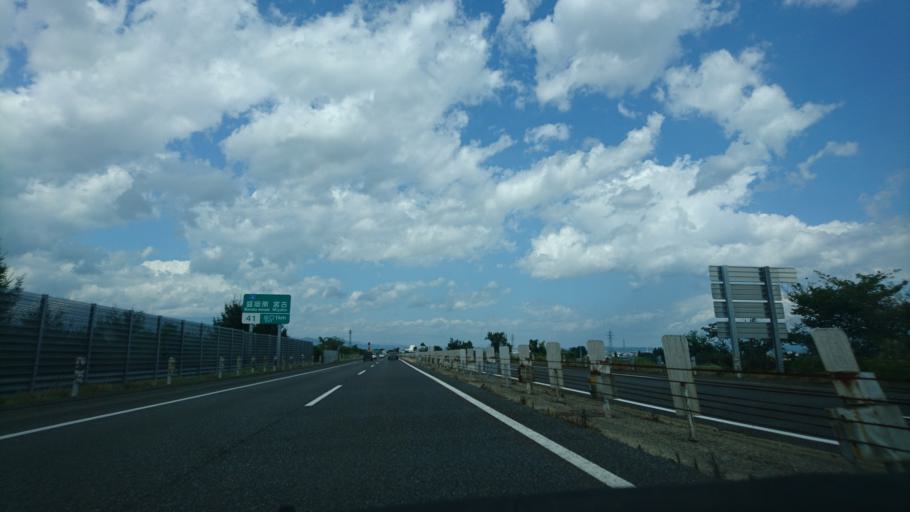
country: JP
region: Iwate
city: Morioka-shi
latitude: 39.6409
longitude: 141.1255
